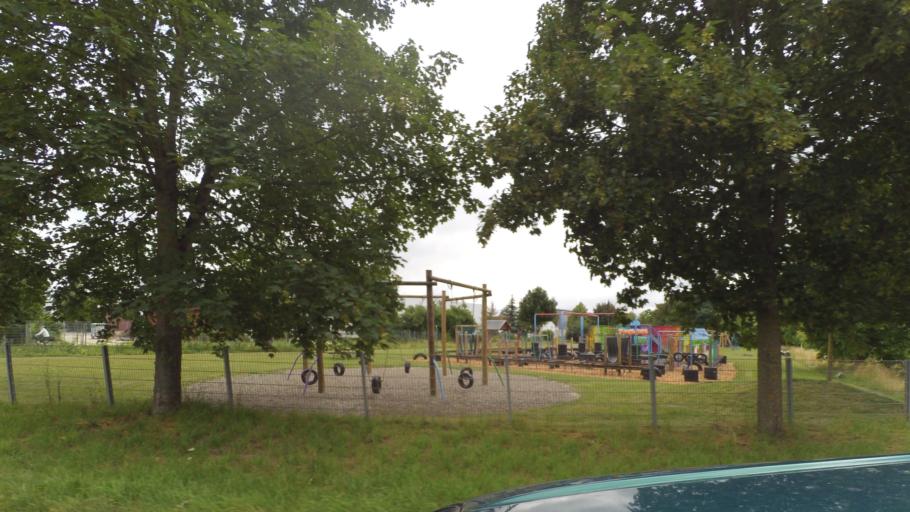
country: DE
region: Baden-Wuerttemberg
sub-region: Tuebingen Region
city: Langenau
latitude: 48.4907
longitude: 10.1096
